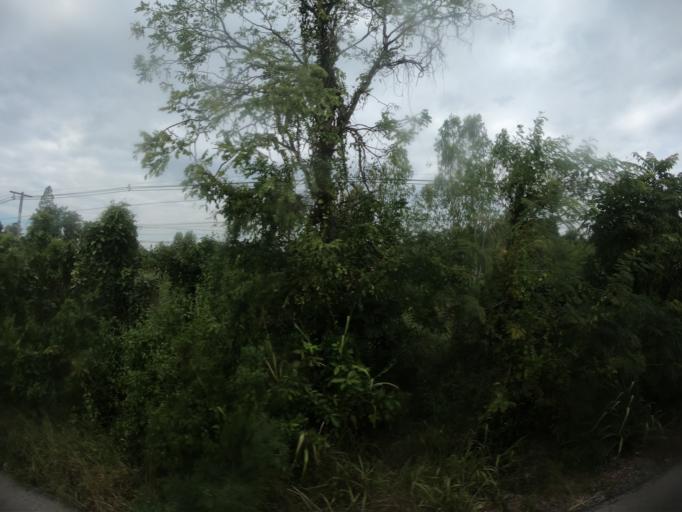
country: TH
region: Maha Sarakham
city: Kantharawichai
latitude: 16.3375
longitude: 103.2228
